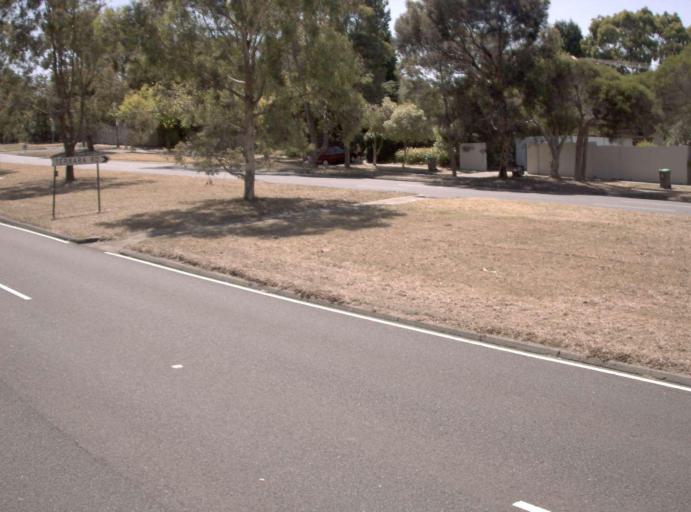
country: AU
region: Victoria
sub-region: Whitehorse
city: Vermont South
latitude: -37.8580
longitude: 145.1916
